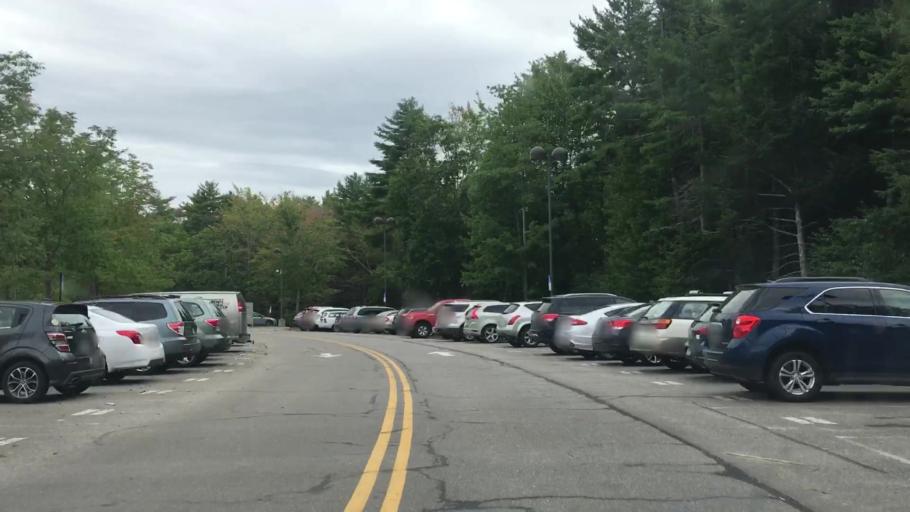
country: US
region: Maine
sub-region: Sagadahoc County
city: Bath
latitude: 43.9057
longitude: -69.8920
